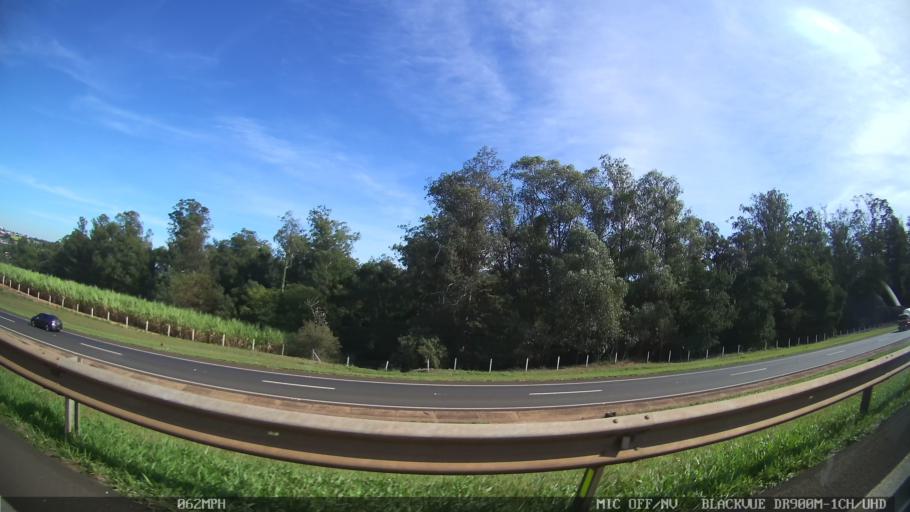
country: BR
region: Sao Paulo
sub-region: Araras
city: Araras
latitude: -22.3379
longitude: -47.3908
